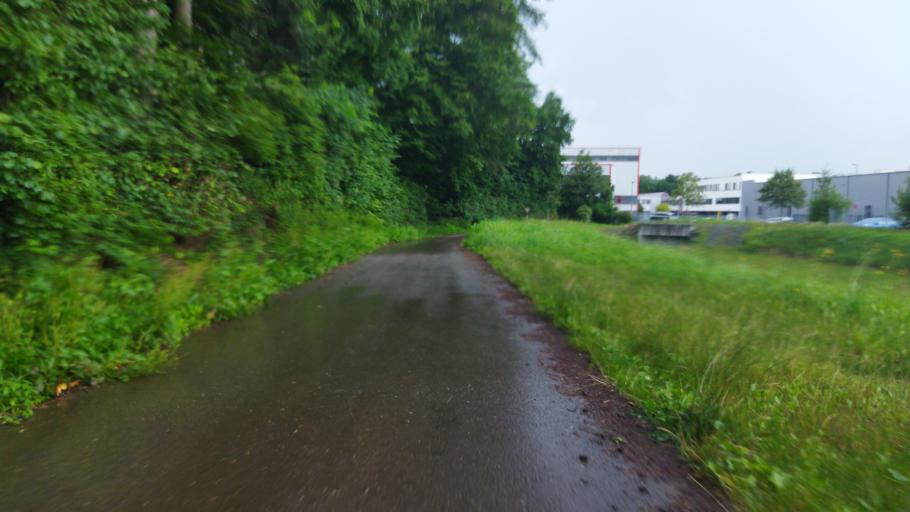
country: DE
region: Baden-Wuerttemberg
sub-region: Regierungsbezirk Stuttgart
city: Kirchardt
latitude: 49.2010
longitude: 9.0053
